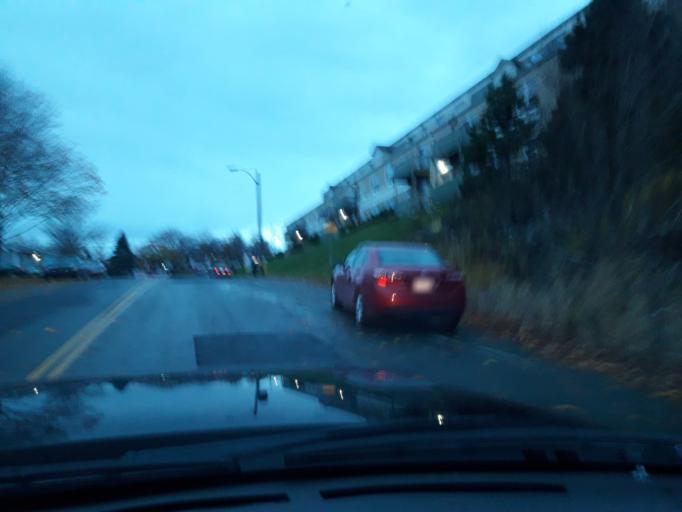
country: CA
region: Newfoundland and Labrador
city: St. John's
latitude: 47.5693
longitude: -52.7488
